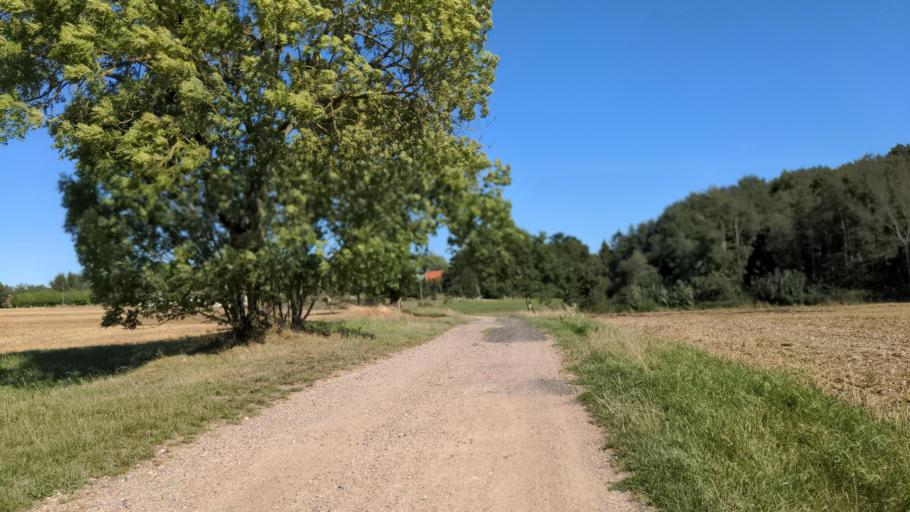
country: DE
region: Mecklenburg-Vorpommern
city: Klutz
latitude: 53.9791
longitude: 11.1364
